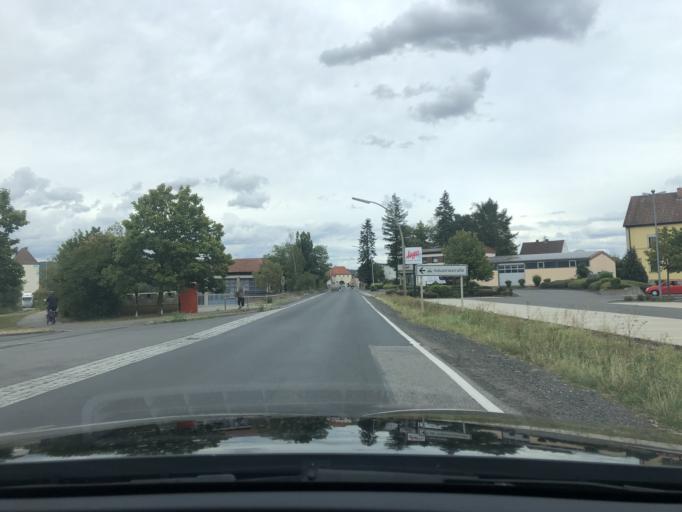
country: DE
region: Bavaria
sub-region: Regierungsbezirk Unterfranken
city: Hofheim in Unterfranken
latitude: 50.1320
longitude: 10.5211
